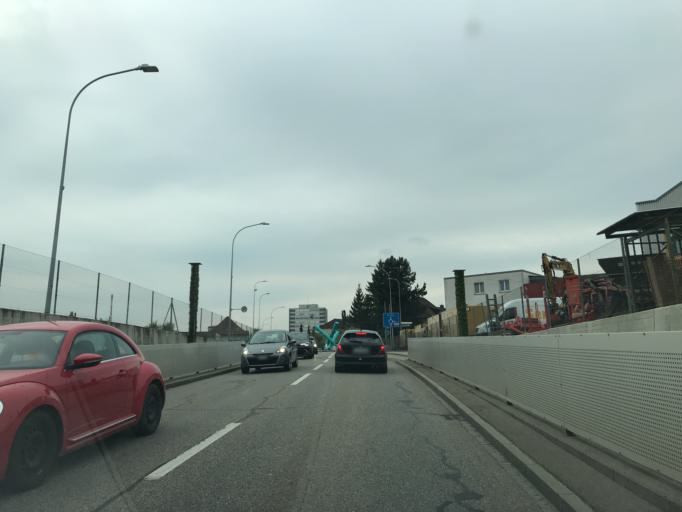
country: CH
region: Bern
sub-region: Oberaargau
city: Langenthal
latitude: 47.2154
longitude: 7.7782
